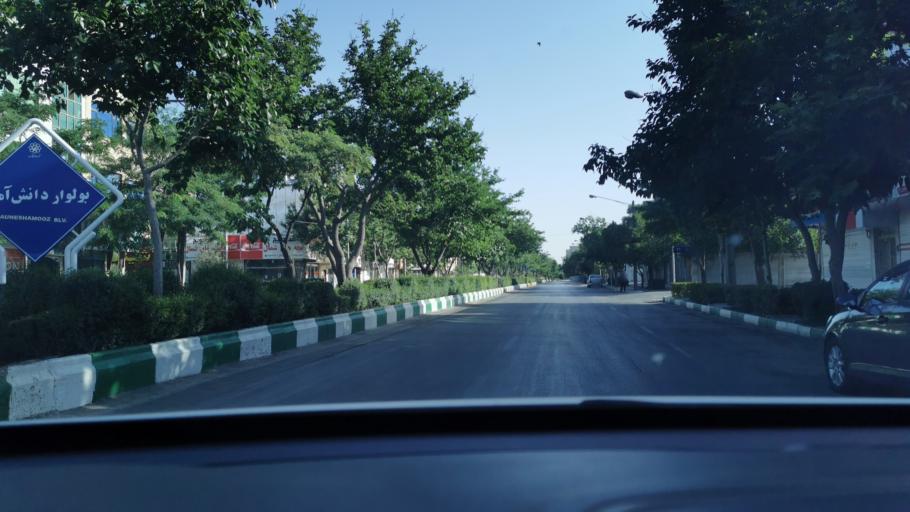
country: IR
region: Razavi Khorasan
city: Mashhad
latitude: 36.3340
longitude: 59.5122
